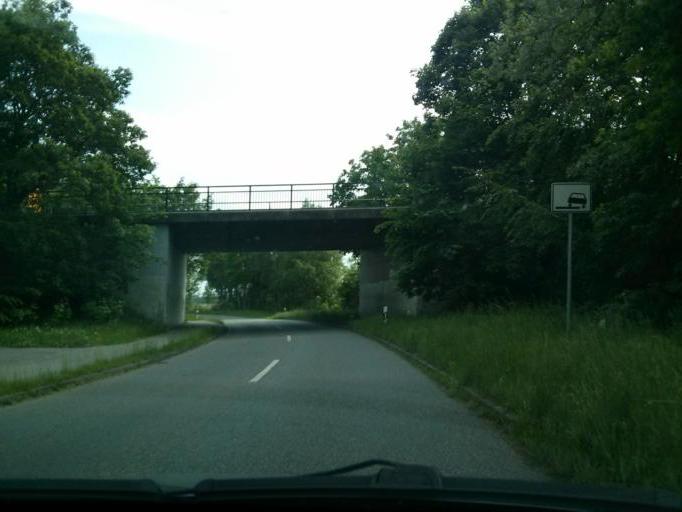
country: DE
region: Lower Saxony
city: Loxstedt
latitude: 53.4944
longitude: 8.6376
